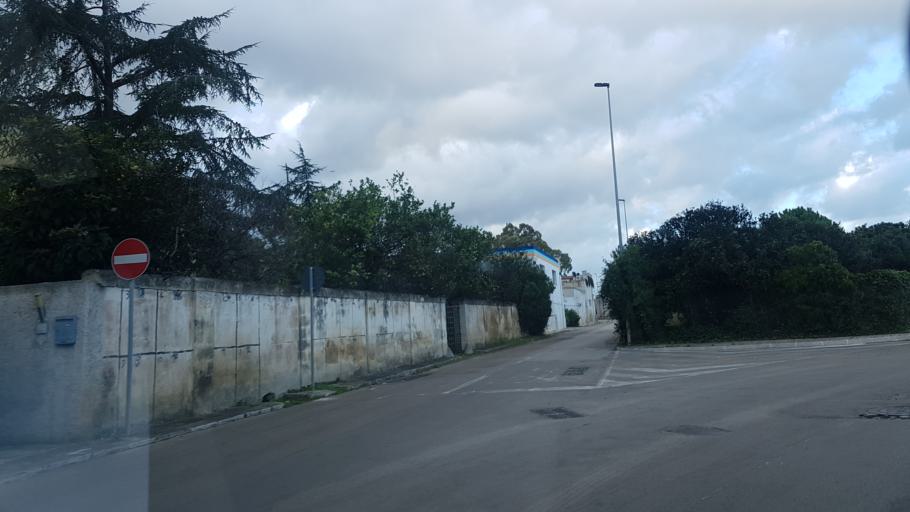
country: IT
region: Apulia
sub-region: Provincia di Brindisi
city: San Pietro Vernotico
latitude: 40.4892
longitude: 18.0014
